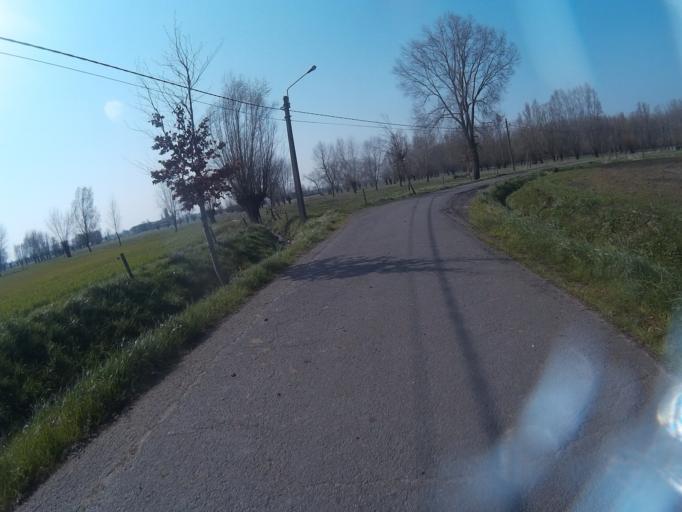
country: BE
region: Flanders
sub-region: Provincie Oost-Vlaanderen
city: Aalter
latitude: 51.1172
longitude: 3.4959
